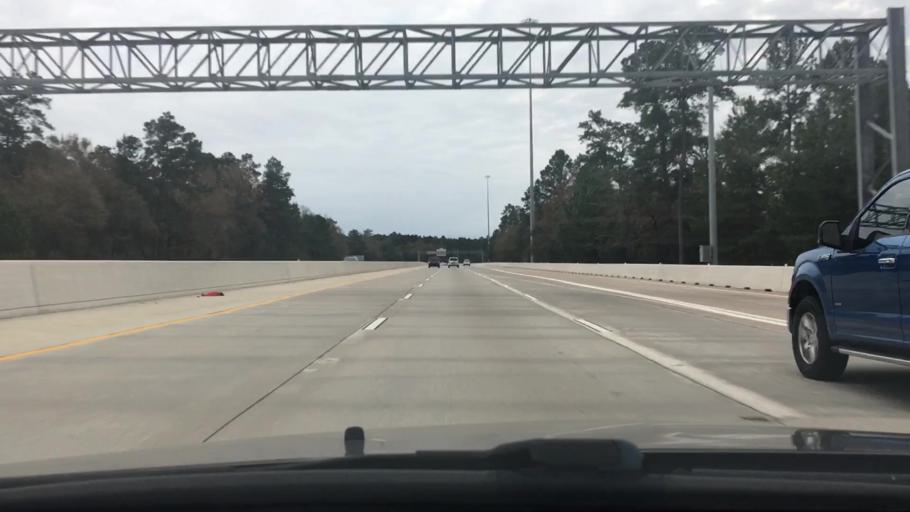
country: US
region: Texas
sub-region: Harris County
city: Spring
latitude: 30.0841
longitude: -95.4120
